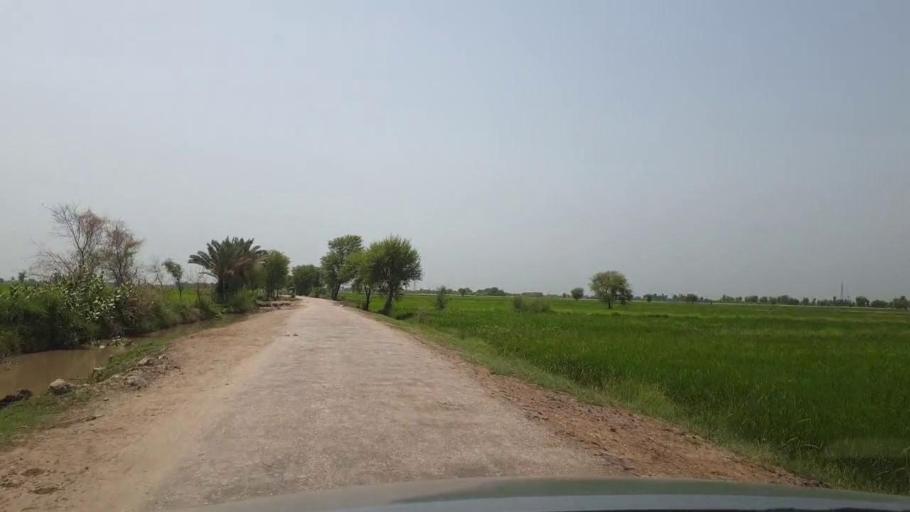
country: PK
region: Sindh
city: Madeji
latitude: 27.7813
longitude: 68.4323
